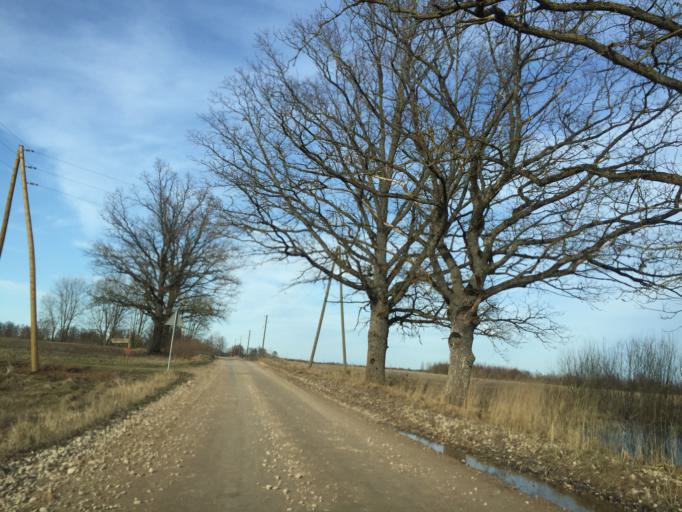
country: LV
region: Kegums
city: Kegums
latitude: 56.8018
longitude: 24.7717
